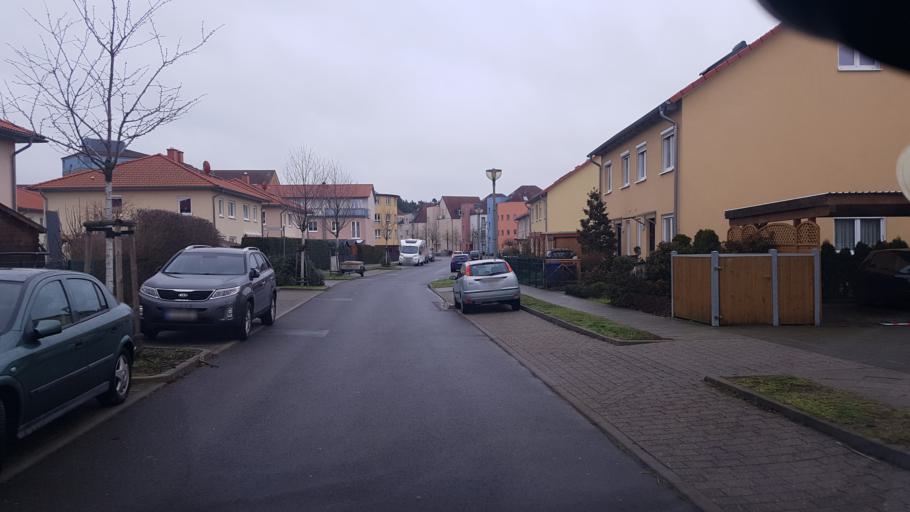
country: DE
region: Berlin
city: Wannsee
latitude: 52.3589
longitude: 13.1337
